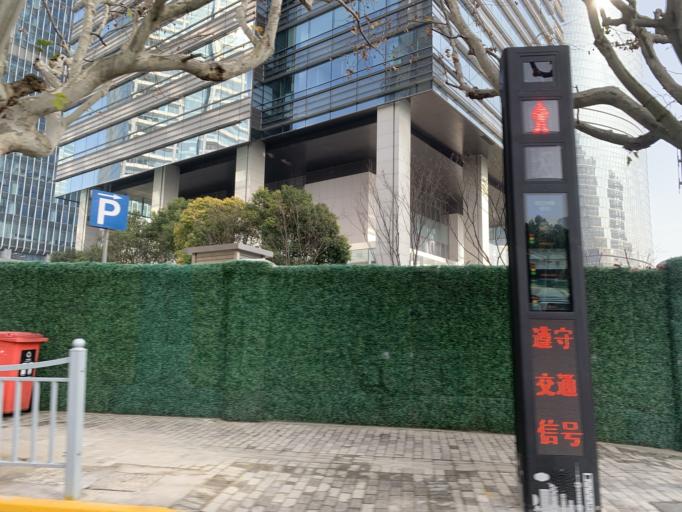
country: CN
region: Shanghai Shi
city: Hongkou
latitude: 31.2349
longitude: 121.4986
